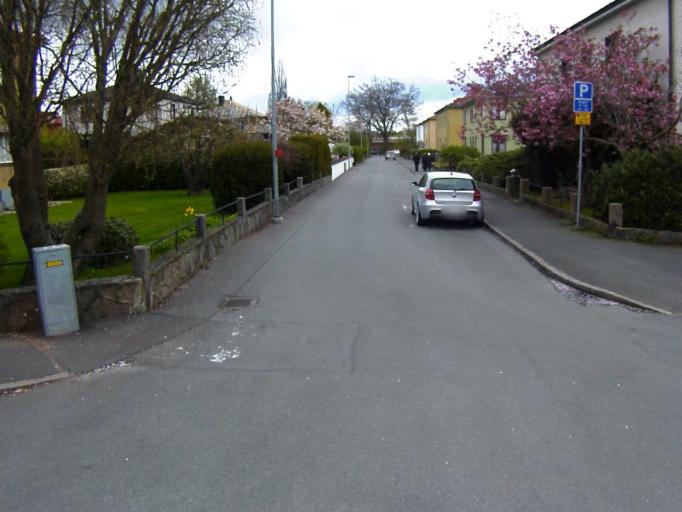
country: SE
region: Skane
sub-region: Kristianstads Kommun
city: Kristianstad
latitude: 56.0258
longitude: 14.1645
